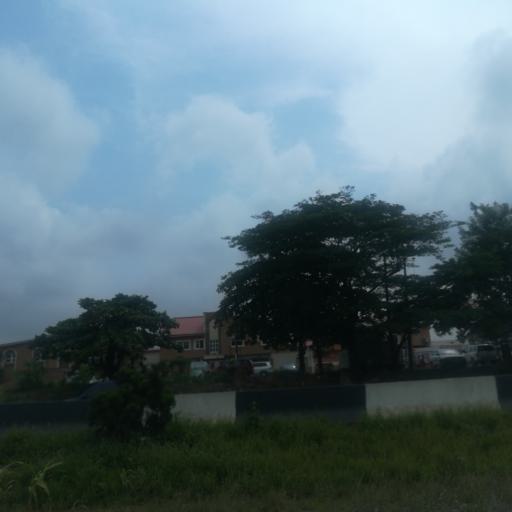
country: NG
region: Lagos
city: Ikeja
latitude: 6.6149
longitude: 3.3665
